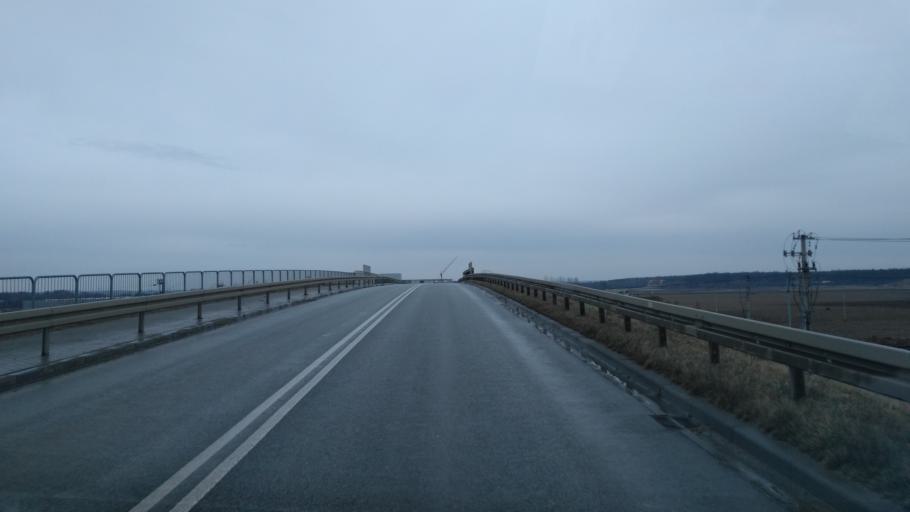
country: PL
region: Subcarpathian Voivodeship
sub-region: Powiat debicki
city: Brzeznica
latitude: 50.0649
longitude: 21.4755
